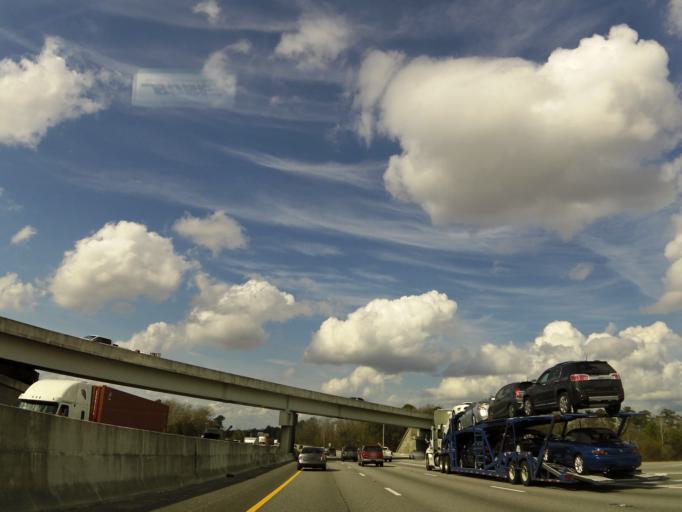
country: US
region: South Carolina
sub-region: Berkeley County
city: Hanahan
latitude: 32.9398
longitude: -80.0502
